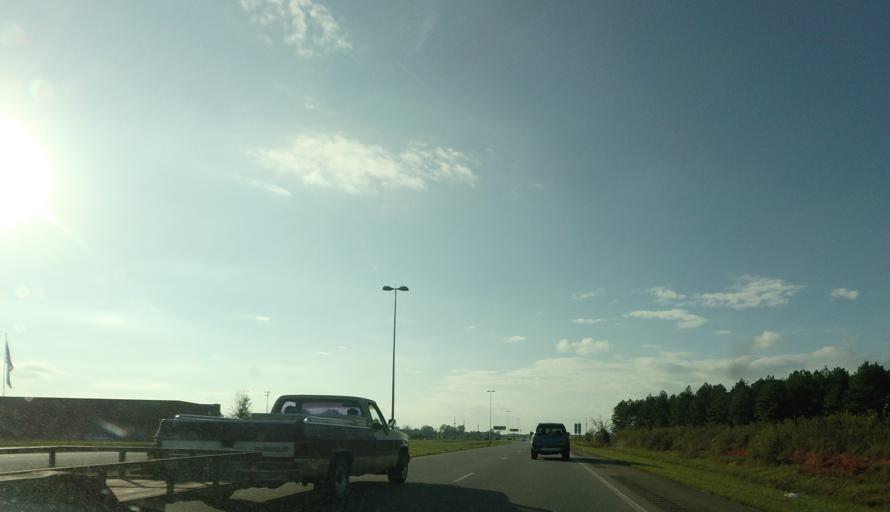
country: US
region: Georgia
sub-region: Houston County
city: Centerville
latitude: 32.5800
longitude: -83.7169
